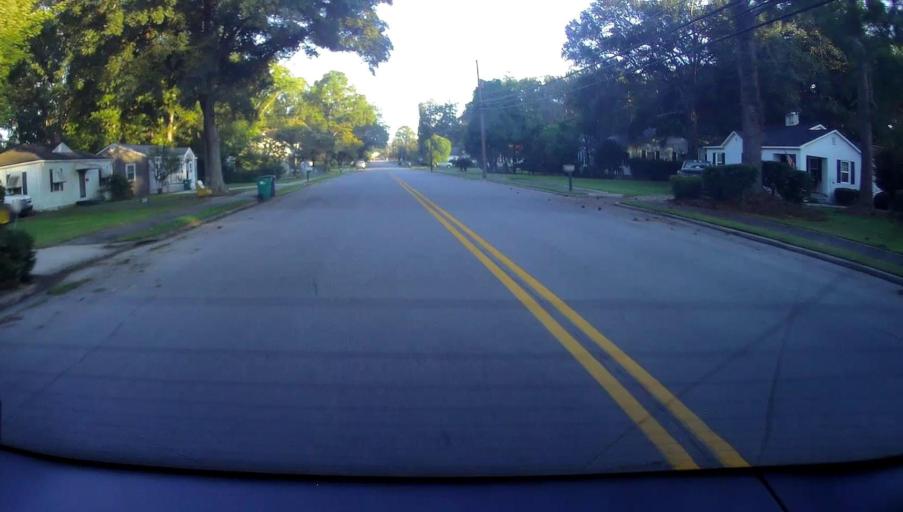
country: US
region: Georgia
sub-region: Bleckley County
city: Cochran
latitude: 32.3853
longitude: -83.3510
